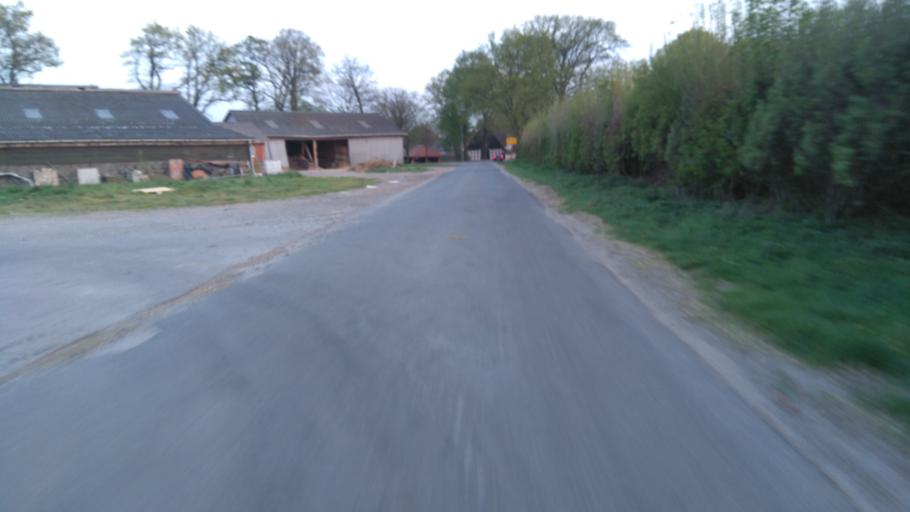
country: DE
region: Lower Saxony
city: Bargstedt
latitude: 53.4699
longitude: 9.4744
